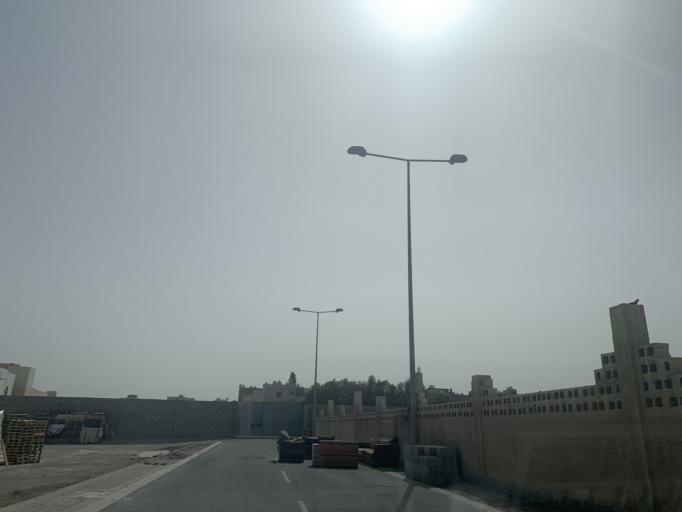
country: BH
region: Northern
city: Sitrah
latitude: 26.1697
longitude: 50.6247
